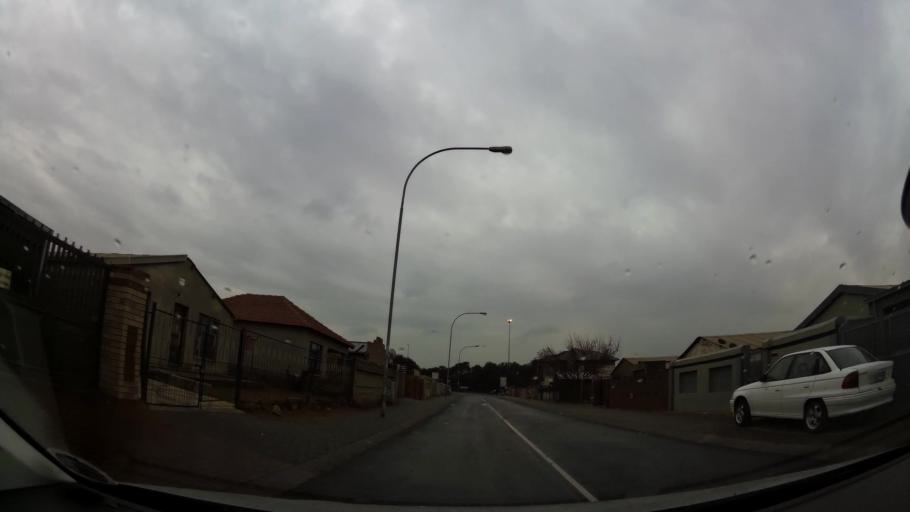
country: ZA
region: Gauteng
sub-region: City of Johannesburg Metropolitan Municipality
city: Soweto
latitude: -26.2462
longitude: 27.8670
